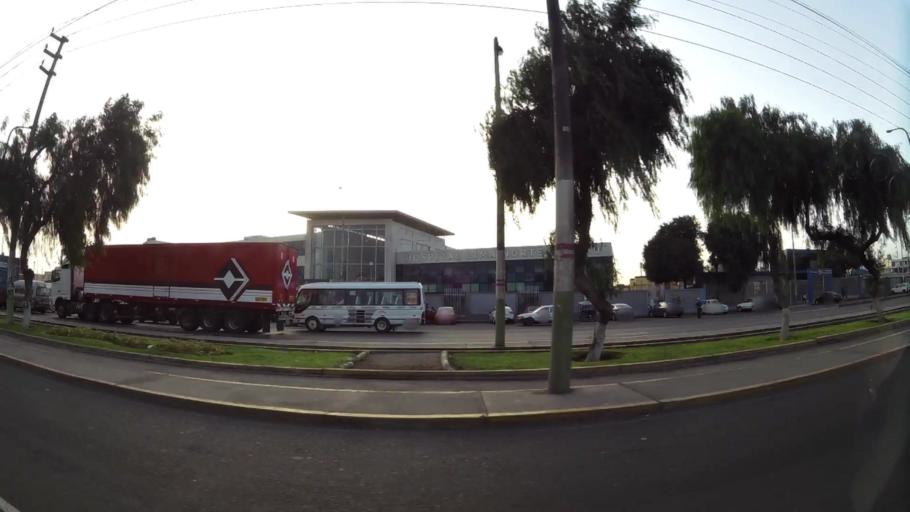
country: PE
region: Callao
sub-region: Callao
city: Callao
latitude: -12.0161
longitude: -77.0974
